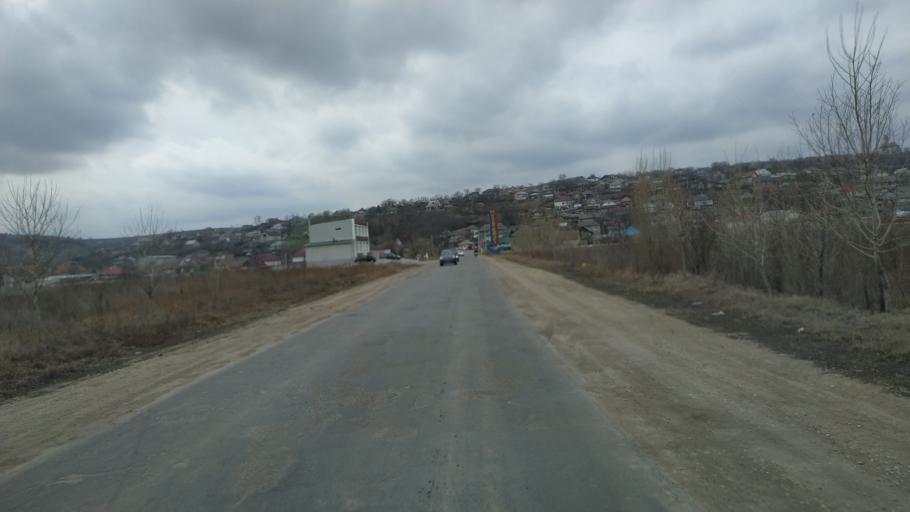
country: MD
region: Laloveni
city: Ialoveni
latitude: 46.8757
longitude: 28.7648
